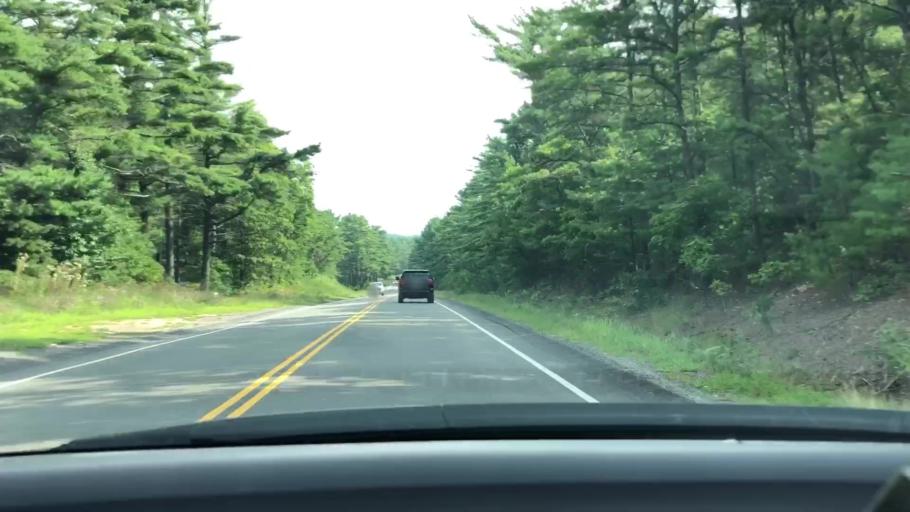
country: US
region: Massachusetts
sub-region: Plymouth County
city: White Island Shores
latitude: 41.8801
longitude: -70.5952
